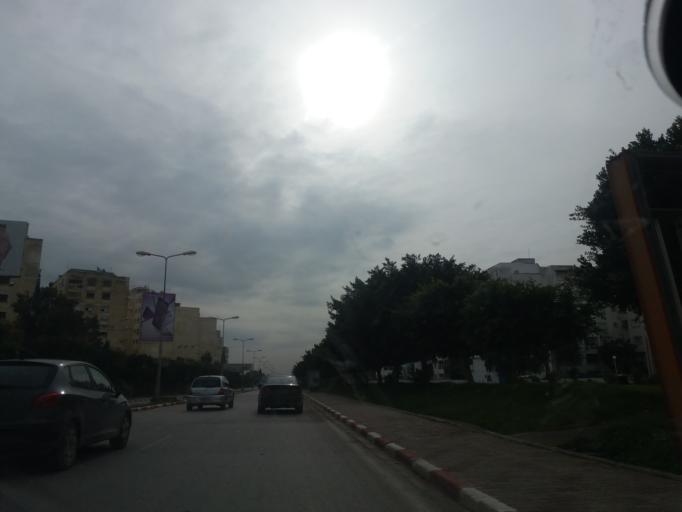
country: TN
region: Tunis
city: Tunis
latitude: 36.8459
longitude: 10.1615
